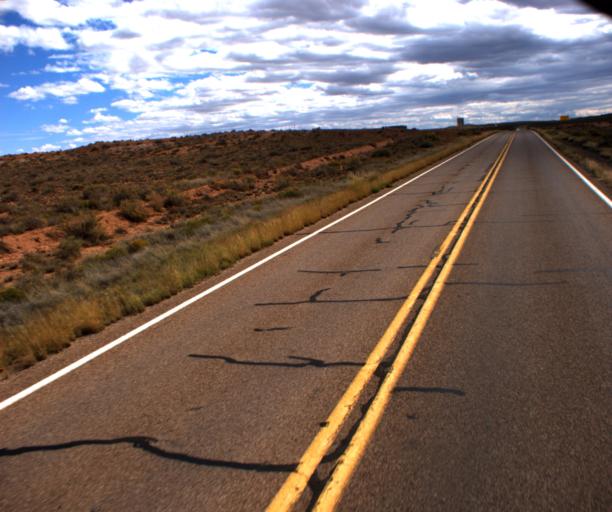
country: US
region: Arizona
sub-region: Navajo County
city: Holbrook
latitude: 34.8630
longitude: -110.1566
